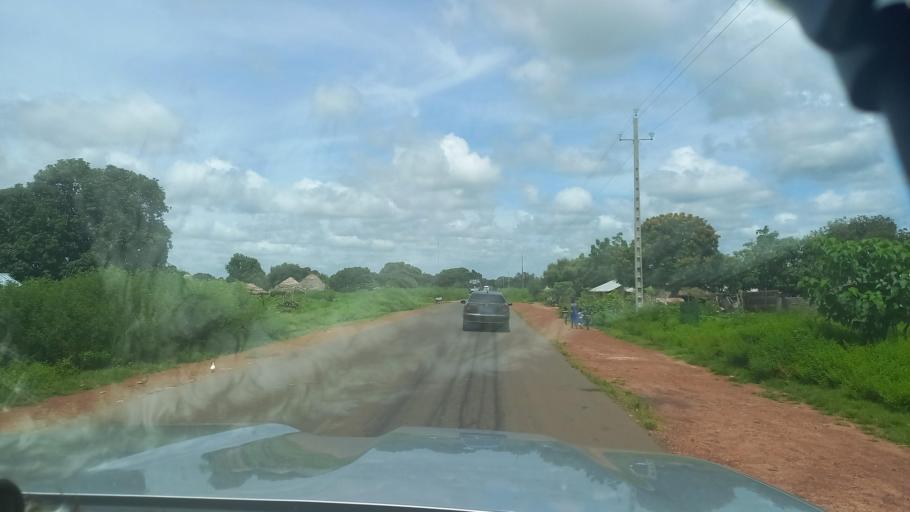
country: GM
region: Lower River
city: Kaiaf
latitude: 13.1990
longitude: -15.5521
